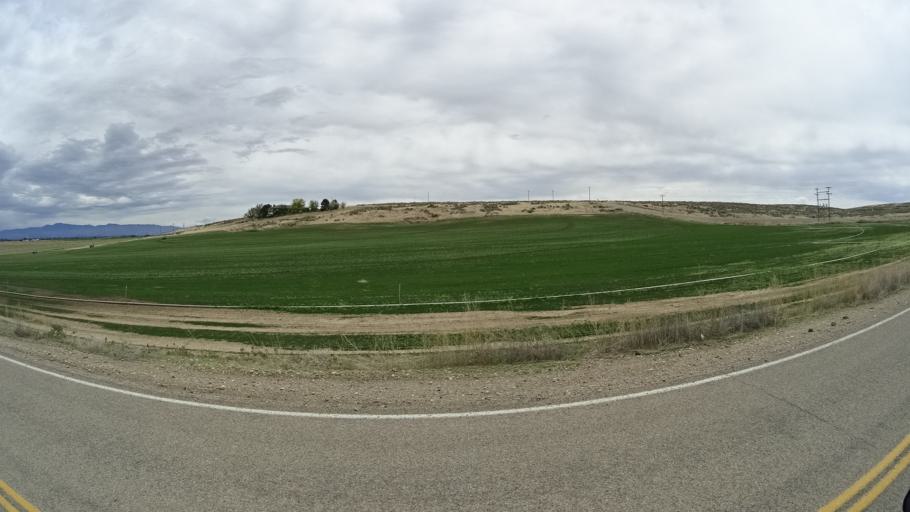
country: US
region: Idaho
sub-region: Ada County
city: Kuna
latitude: 43.4605
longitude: -116.4442
